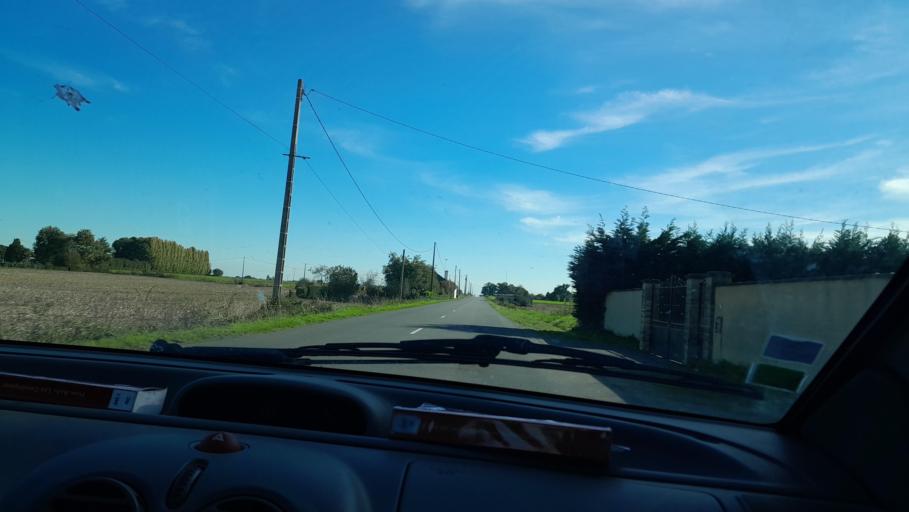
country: FR
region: Brittany
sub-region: Departement d'Ille-et-Vilaine
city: Argentre-du-Plessis
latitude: 48.0191
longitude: -1.1362
